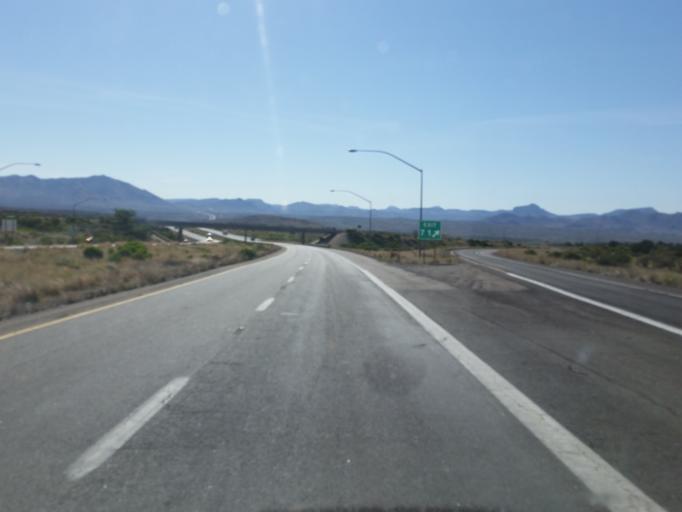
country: US
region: Arizona
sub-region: Mohave County
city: New Kingman-Butler
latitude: 35.1593
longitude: -113.6997
